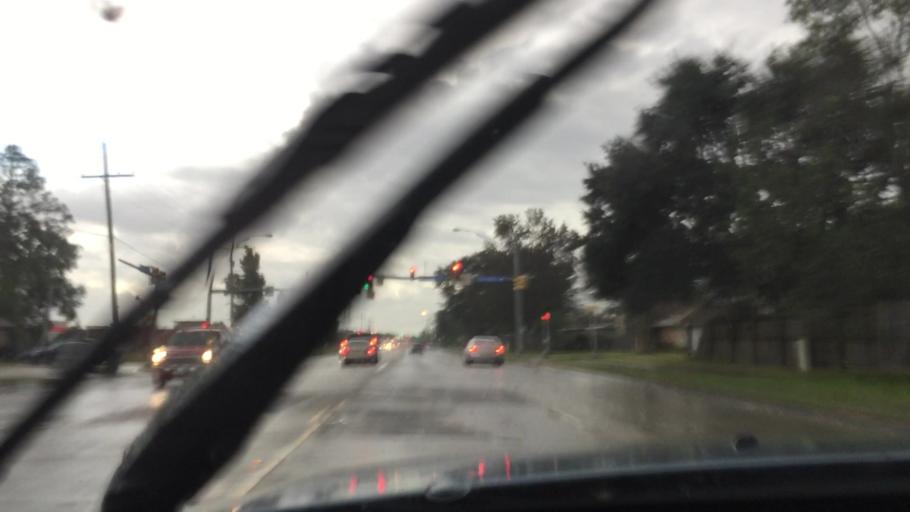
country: US
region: Louisiana
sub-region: East Baton Rouge Parish
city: Monticello
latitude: 30.4474
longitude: -91.0245
